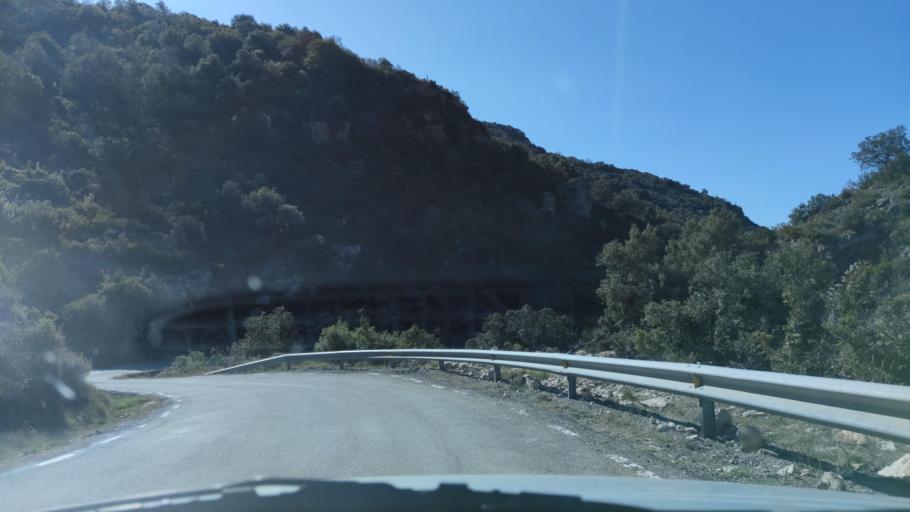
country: ES
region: Catalonia
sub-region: Provincia de Lleida
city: Artesa de Segre
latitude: 42.0100
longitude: 1.0320
